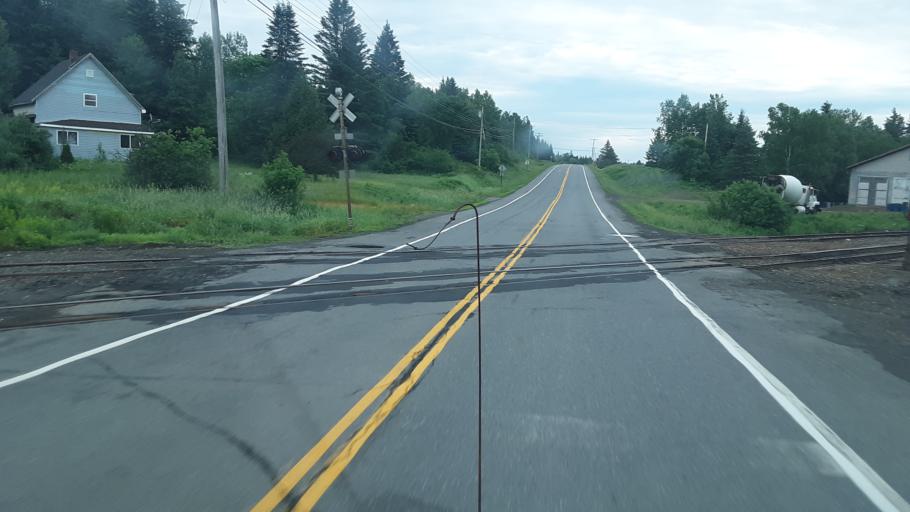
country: US
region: Maine
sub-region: Aroostook County
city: Presque Isle
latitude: 46.5560
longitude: -68.3764
